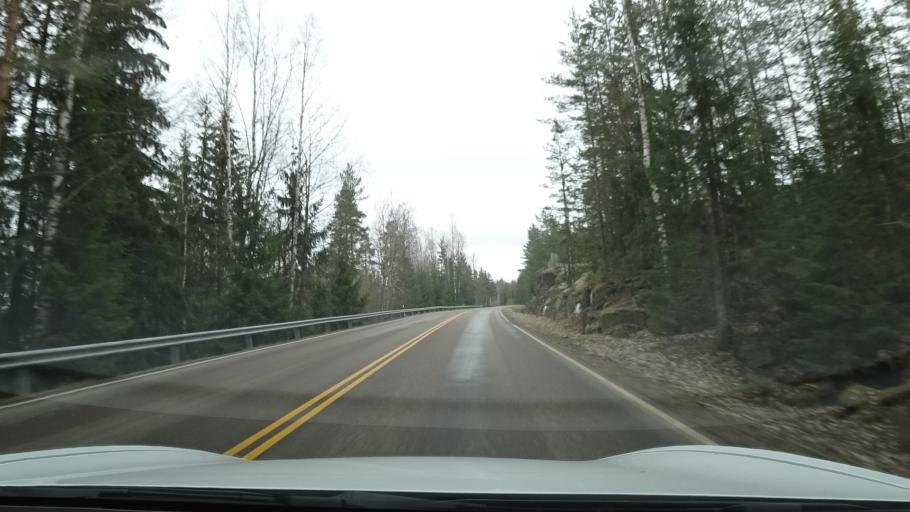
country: FI
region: Uusimaa
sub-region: Porvoo
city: Myrskylae
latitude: 60.7044
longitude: 25.9165
